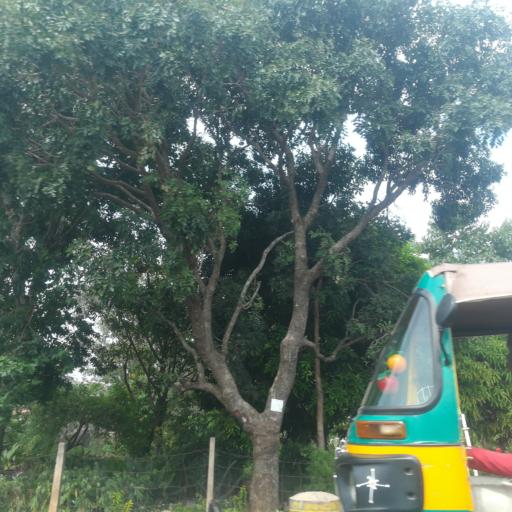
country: NG
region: Plateau
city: Jos
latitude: 9.9098
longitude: 8.8882
